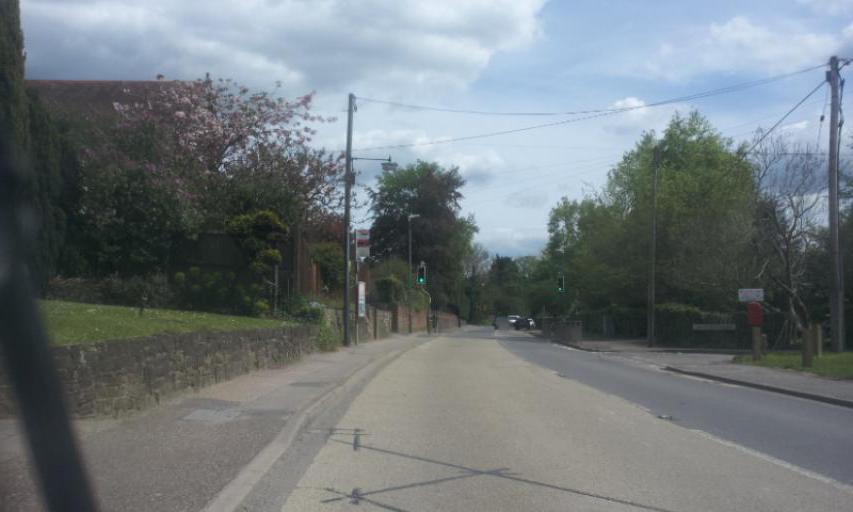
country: GB
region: England
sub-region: Kent
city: Longfield
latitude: 51.3945
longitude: 0.3179
